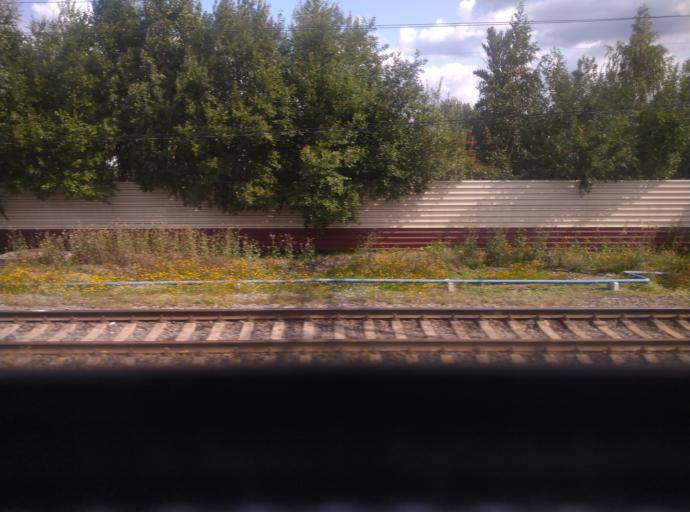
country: RU
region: St.-Petersburg
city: Kolpino
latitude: 59.7549
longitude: 30.6062
